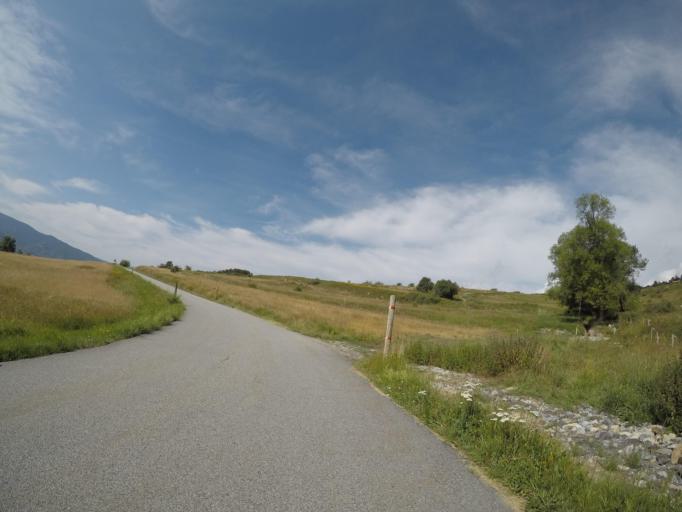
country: ES
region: Catalonia
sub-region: Provincia de Girona
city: Llivia
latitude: 42.4979
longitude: 2.0548
